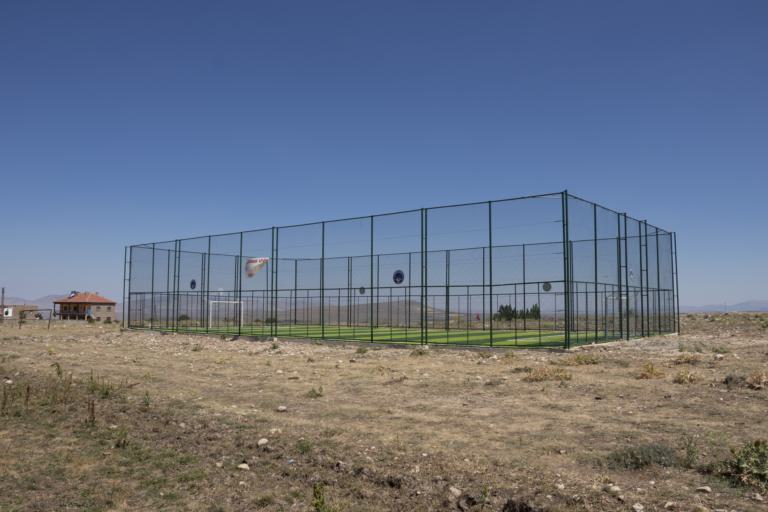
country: TR
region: Kayseri
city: Toklar
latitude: 38.4074
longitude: 36.0868
